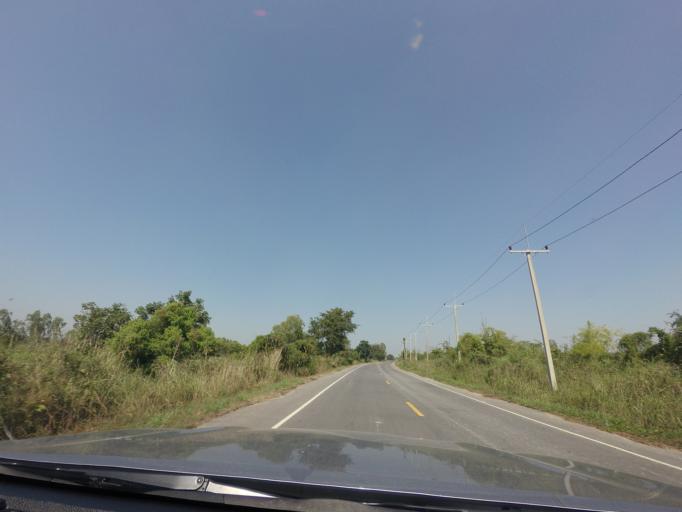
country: TH
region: Sukhothai
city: Sukhothai
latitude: 17.0760
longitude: 99.7908
